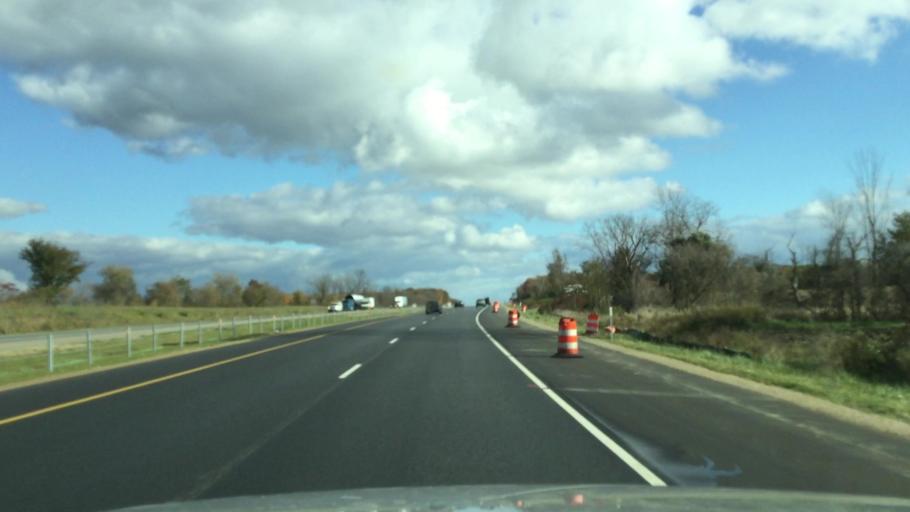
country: US
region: Michigan
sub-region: Van Buren County
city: Decatur
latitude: 42.1956
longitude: -86.0301
